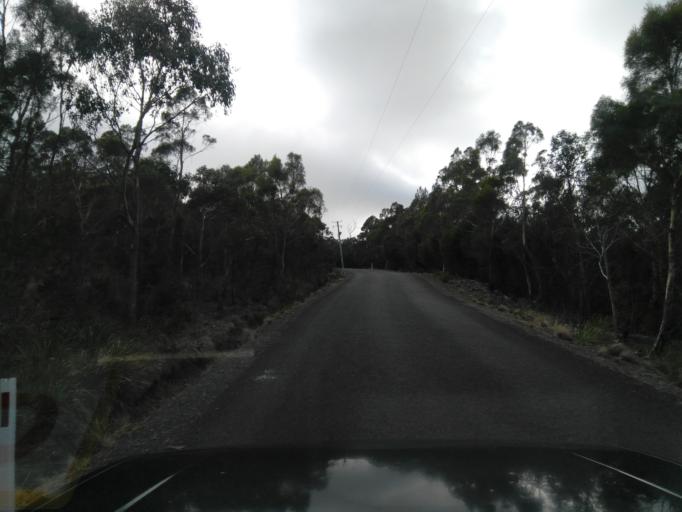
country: AU
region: Tasmania
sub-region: Kingborough
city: Taroona
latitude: -42.9507
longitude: 147.3198
